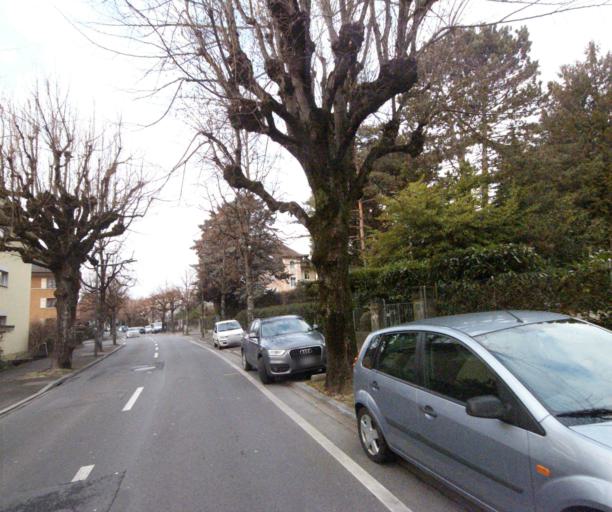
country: CH
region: Vaud
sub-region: Riviera-Pays-d'Enhaut District
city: La Tour-de-Peilz
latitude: 46.4609
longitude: 6.8583
